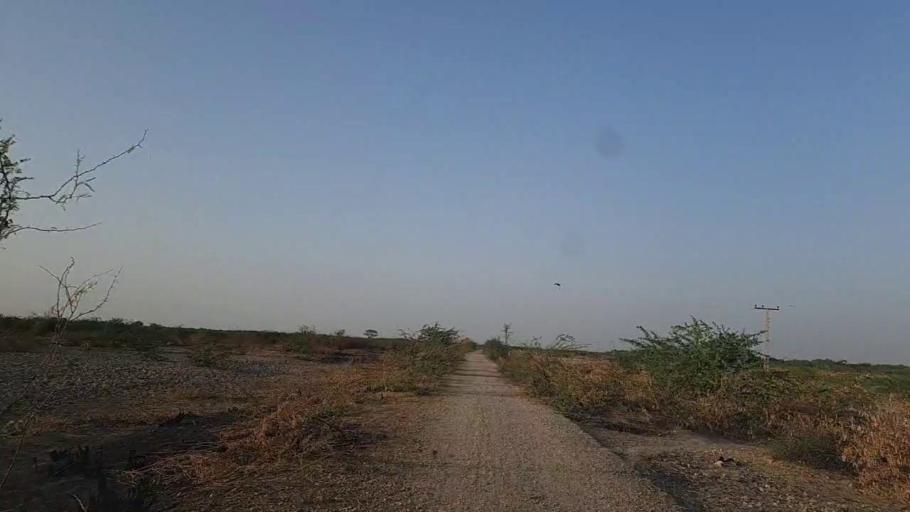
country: PK
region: Sindh
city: Naukot
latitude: 24.6438
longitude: 69.2520
